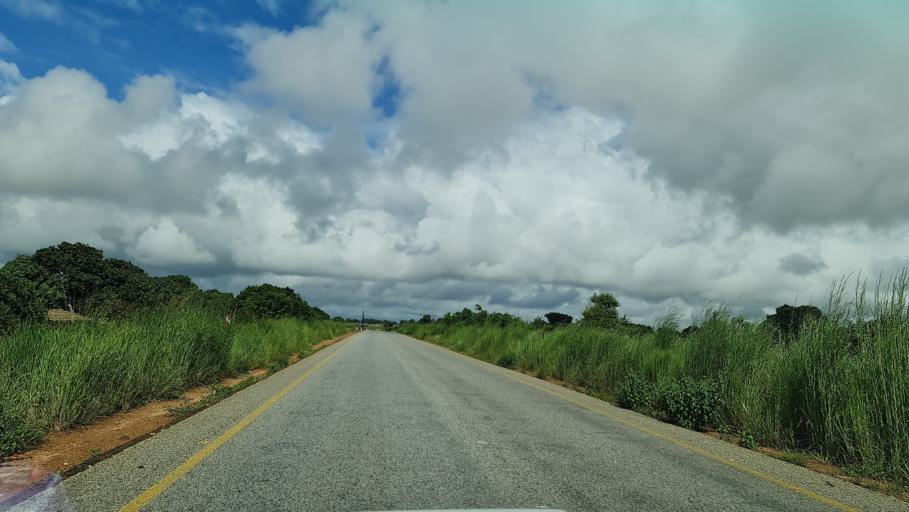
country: MZ
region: Nampula
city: Nampula
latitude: -15.0253
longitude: 38.4660
